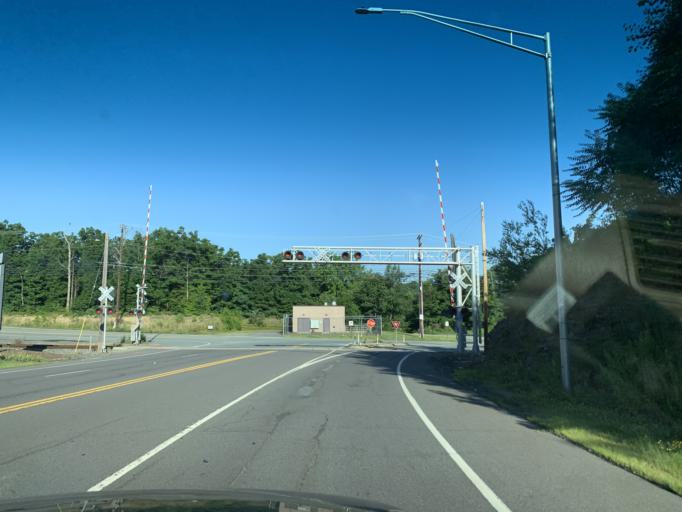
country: US
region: Pennsylvania
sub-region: Lackawanna County
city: Taylor
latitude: 41.3649
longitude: -75.6864
